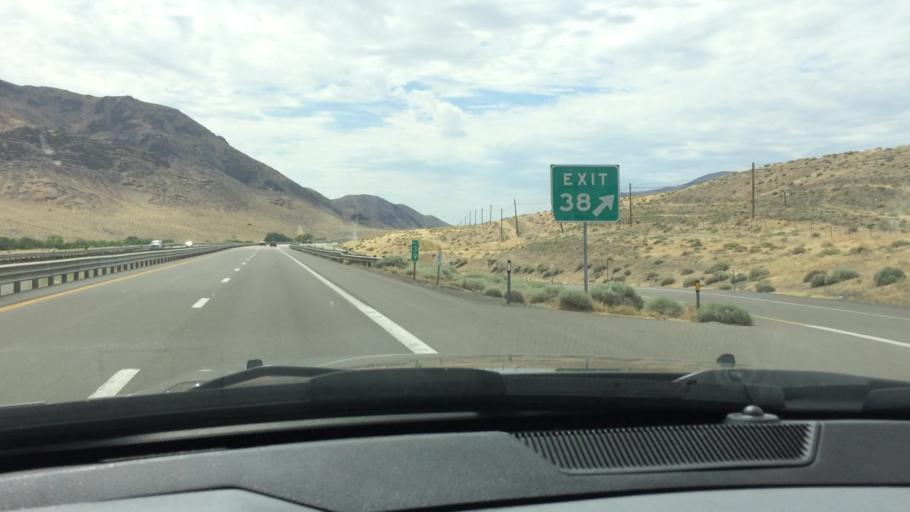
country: US
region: Nevada
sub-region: Lyon County
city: Fernley
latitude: 39.5899
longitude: -119.3890
